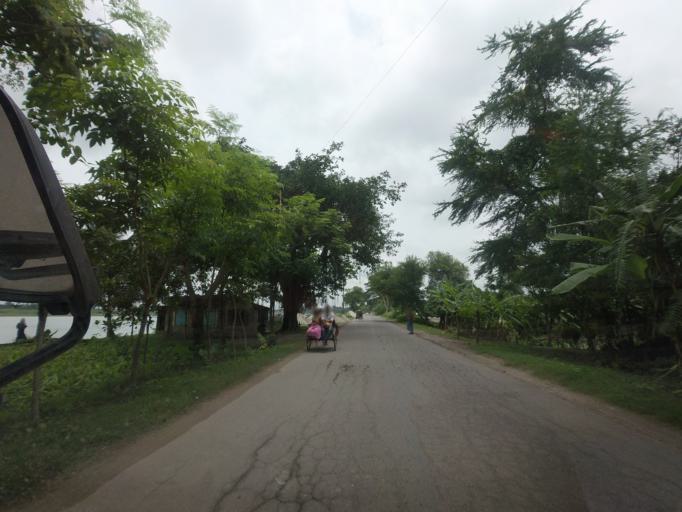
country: BD
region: Khulna
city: Kalia
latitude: 23.2013
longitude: 89.6977
